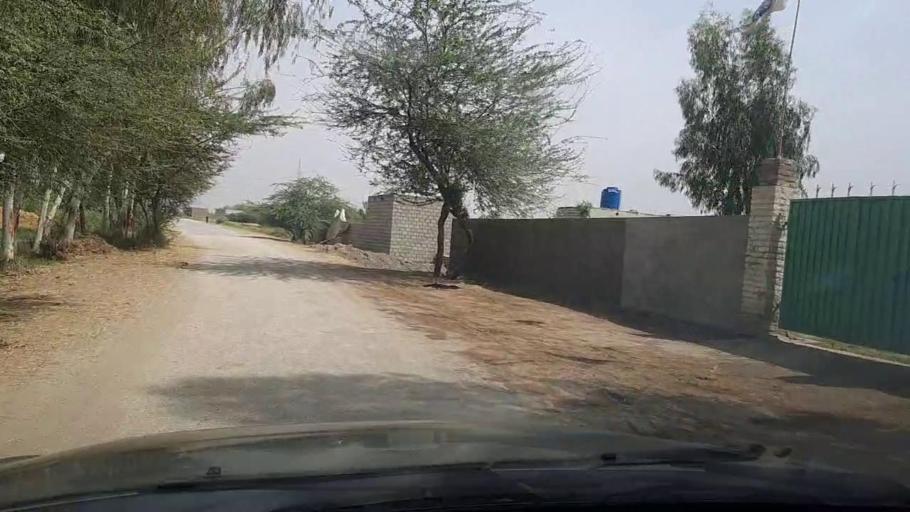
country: PK
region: Sindh
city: Shikarpur
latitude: 27.9253
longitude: 68.6679
